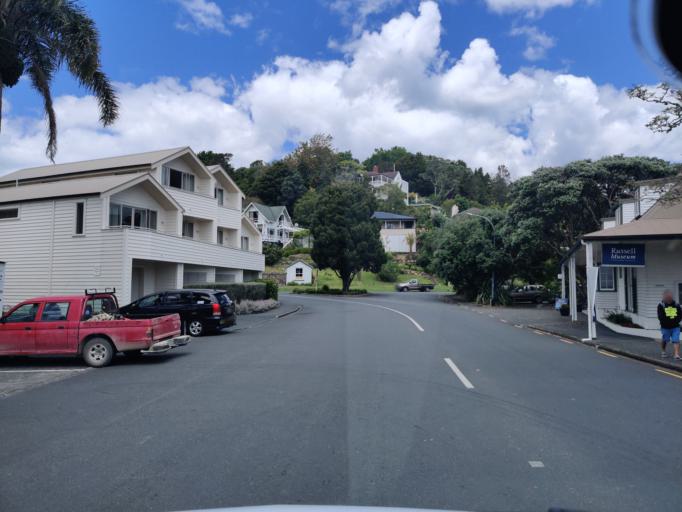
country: NZ
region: Northland
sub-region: Far North District
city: Paihia
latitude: -35.2629
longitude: 174.1226
